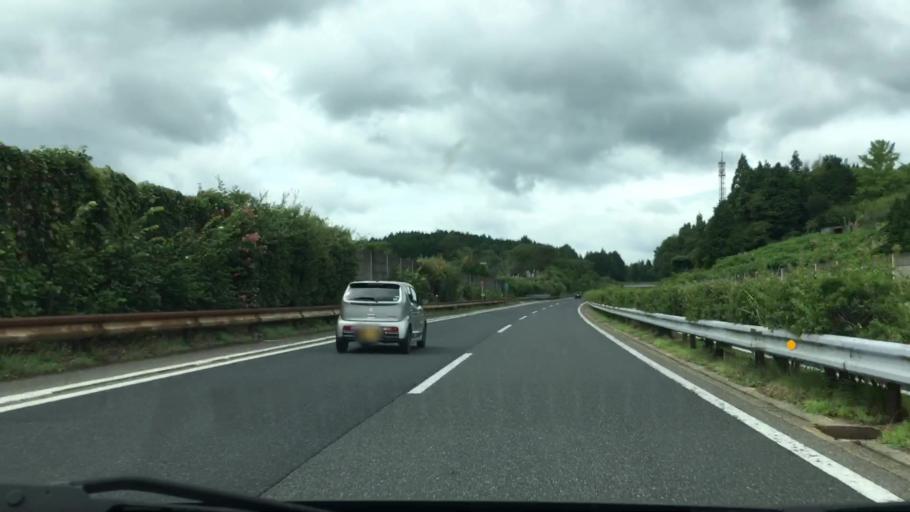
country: JP
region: Okayama
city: Tsuyama
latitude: 35.0613
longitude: 133.8659
